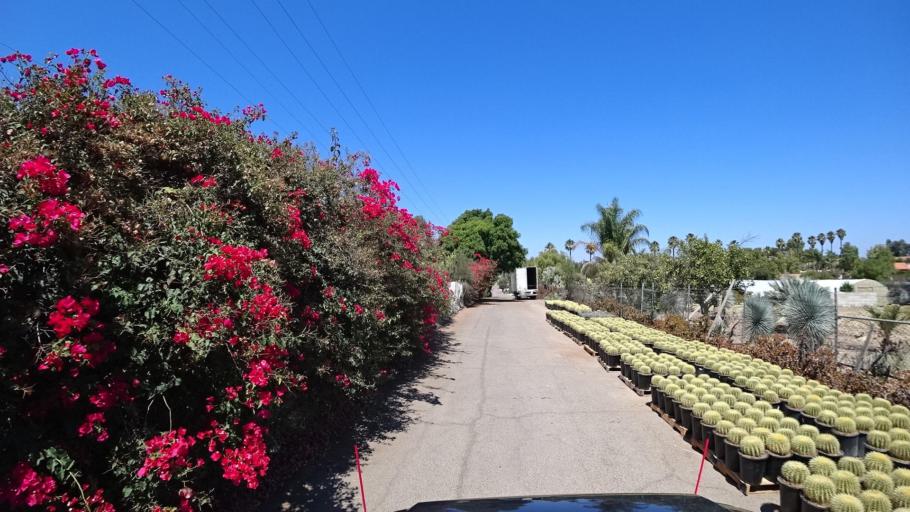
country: US
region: California
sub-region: San Diego County
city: Fallbrook
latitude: 33.3594
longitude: -117.2579
